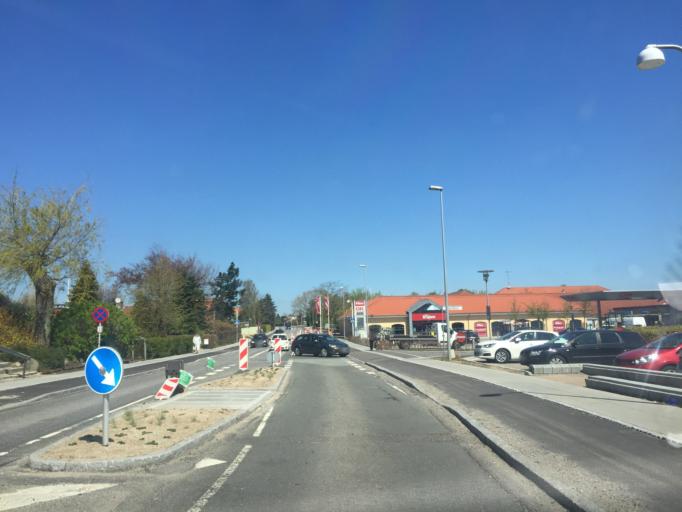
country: DK
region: Capital Region
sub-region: Allerod Kommune
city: Lynge
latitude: 55.8376
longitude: 12.2767
